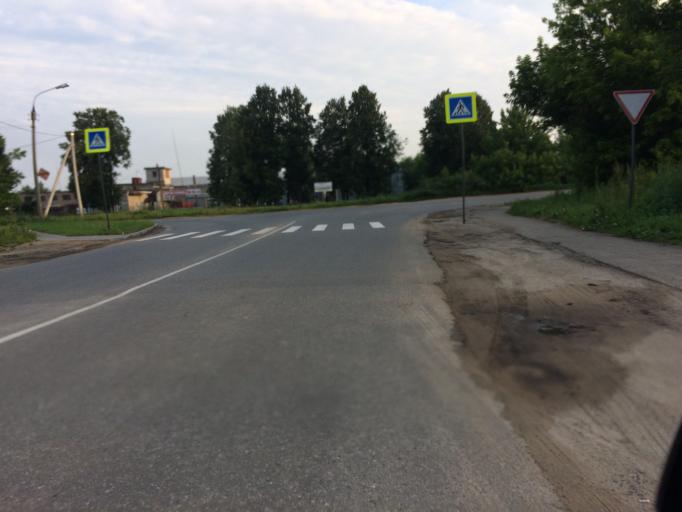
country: RU
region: Mariy-El
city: Yoshkar-Ola
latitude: 56.6479
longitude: 47.9543
